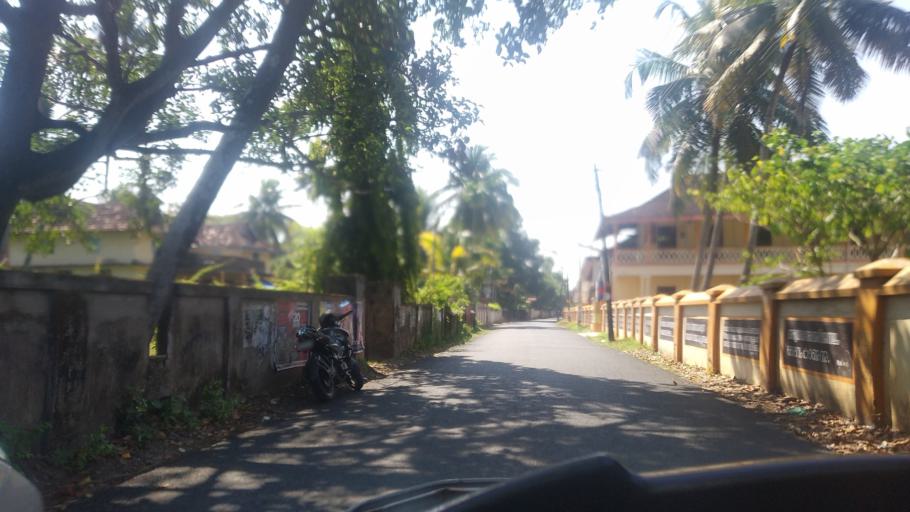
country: IN
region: Kerala
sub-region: Ernakulam
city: Elur
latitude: 10.0441
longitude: 76.2213
